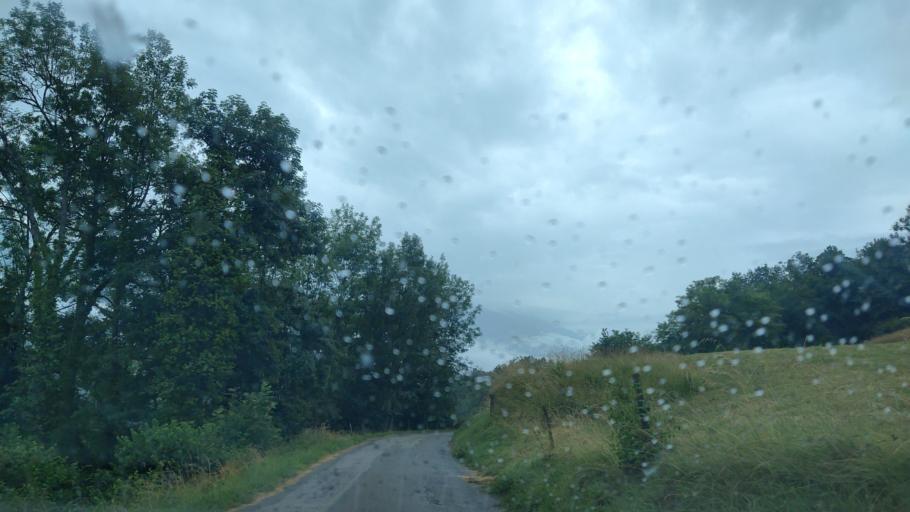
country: FR
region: Rhone-Alpes
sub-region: Departement de la Savoie
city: Coise-Saint-Jean-Pied-Gauthier
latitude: 45.5117
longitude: 6.1503
